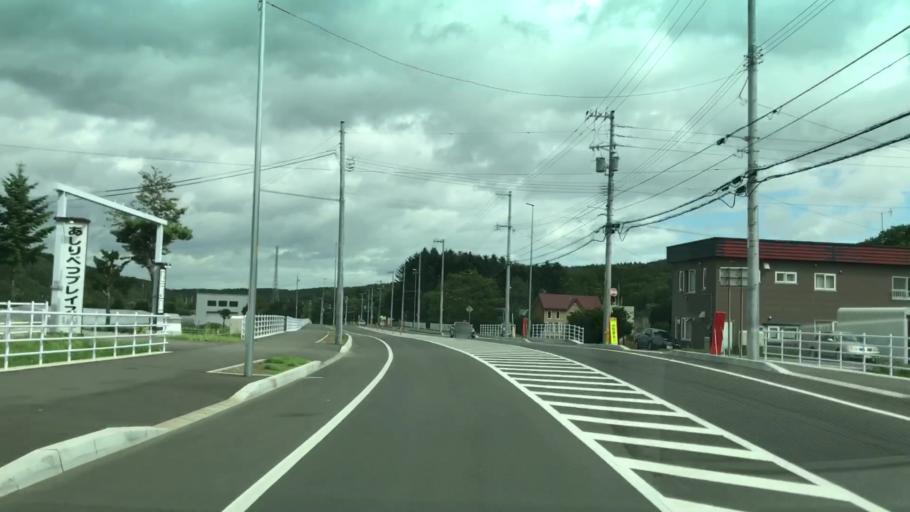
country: JP
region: Hokkaido
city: Kitahiroshima
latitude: 42.9484
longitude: 141.4491
